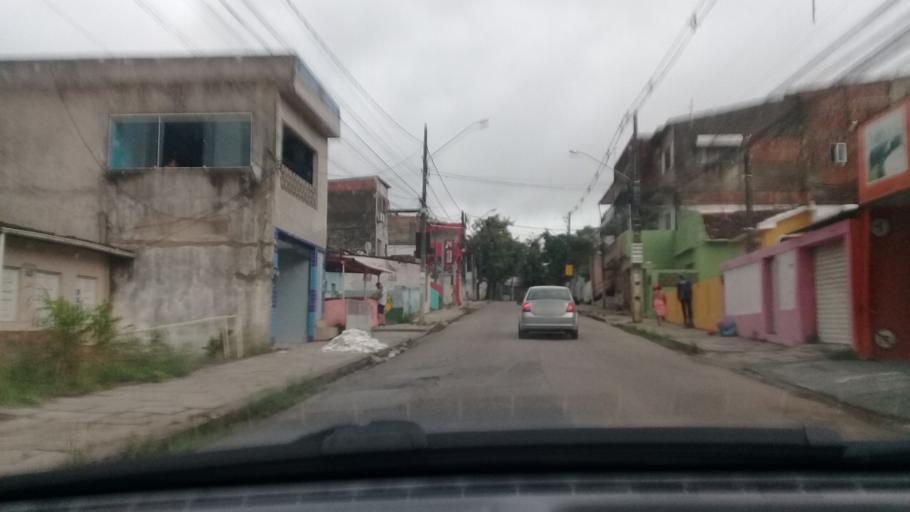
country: BR
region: Pernambuco
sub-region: Moreno
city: Moreno
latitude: -8.1176
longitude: -35.0935
